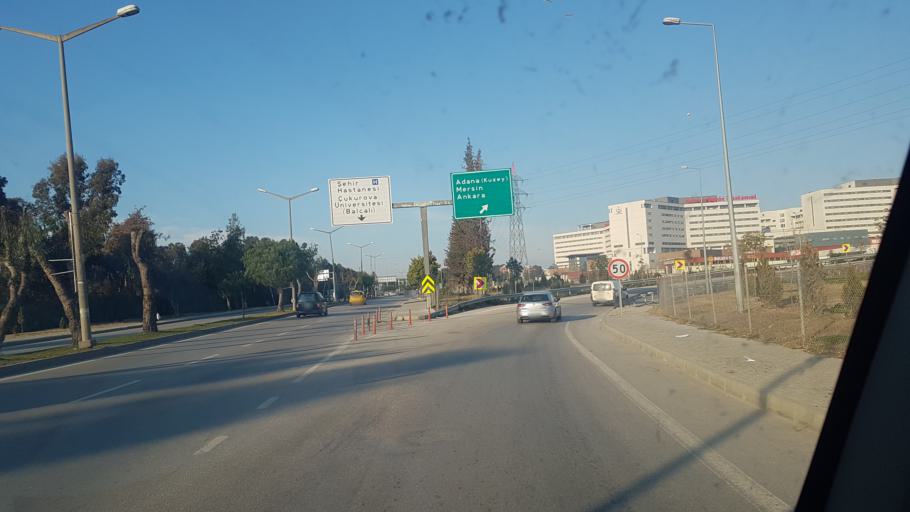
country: TR
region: Adana
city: Adana
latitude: 37.0250
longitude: 35.3440
